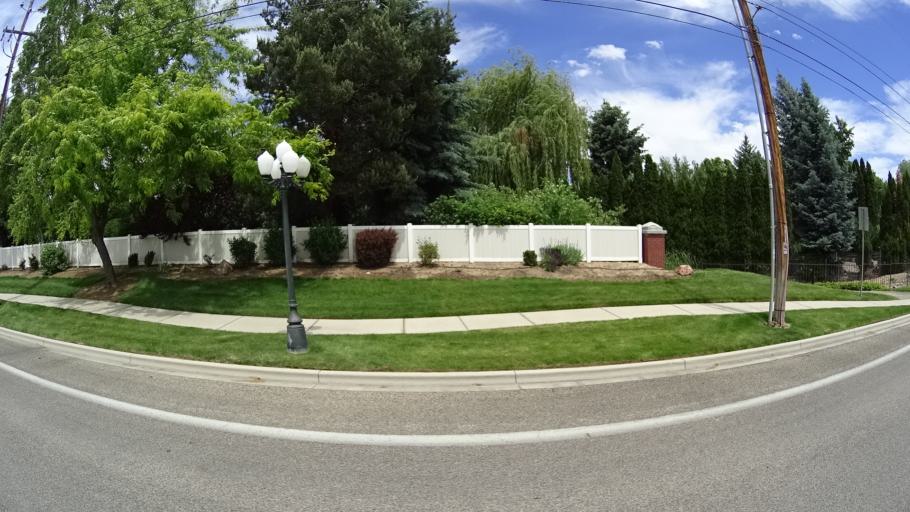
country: US
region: Idaho
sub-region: Ada County
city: Eagle
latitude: 43.6485
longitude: -116.3216
